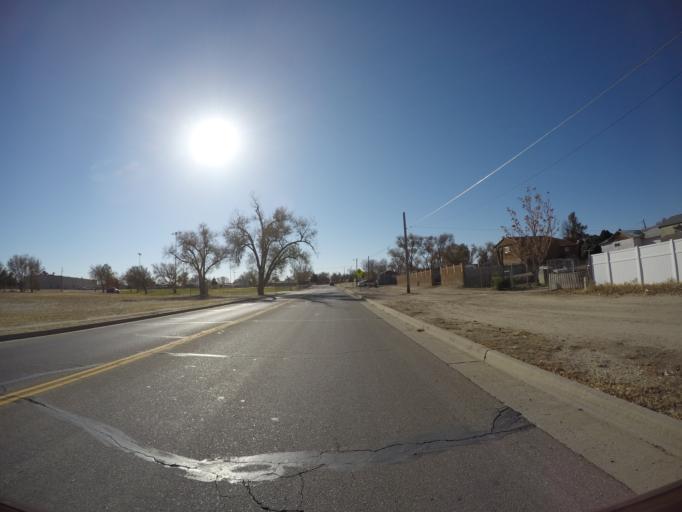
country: US
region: Colorado
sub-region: Otero County
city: La Junta
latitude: 37.9846
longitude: -103.5325
